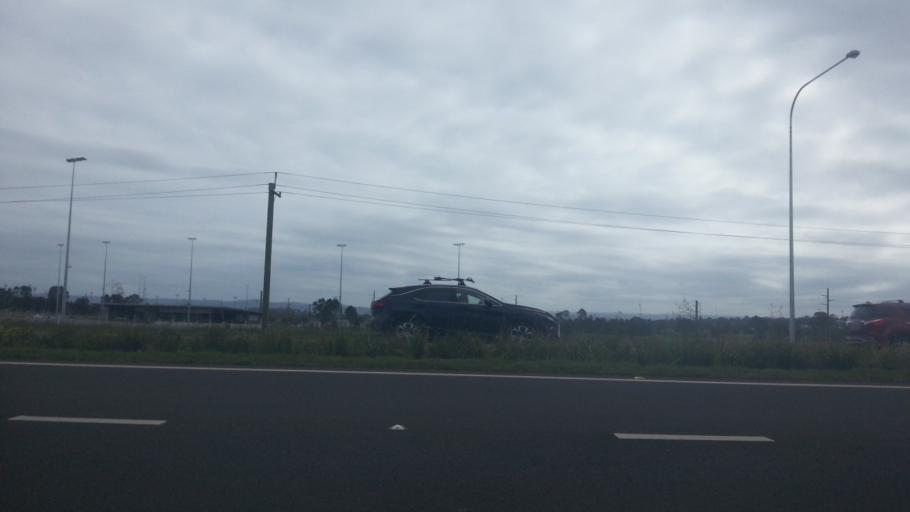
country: AU
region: New South Wales
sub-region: Camden
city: Narellan
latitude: -34.0309
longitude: 150.7288
